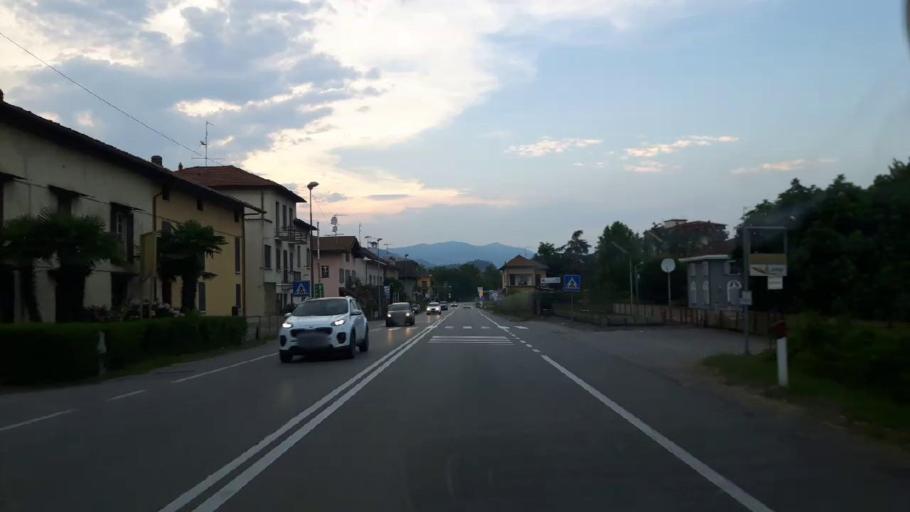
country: IT
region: Piedmont
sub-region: Provincia di Novara
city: Dormelletto
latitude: 45.7429
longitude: 8.5669
